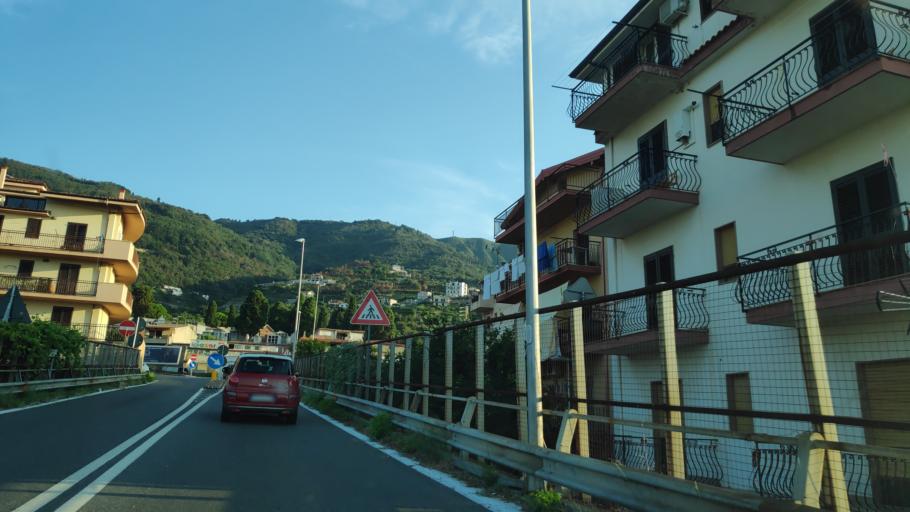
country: IT
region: Calabria
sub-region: Provincia di Reggio Calabria
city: Scilla
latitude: 38.2516
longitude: 15.7205
